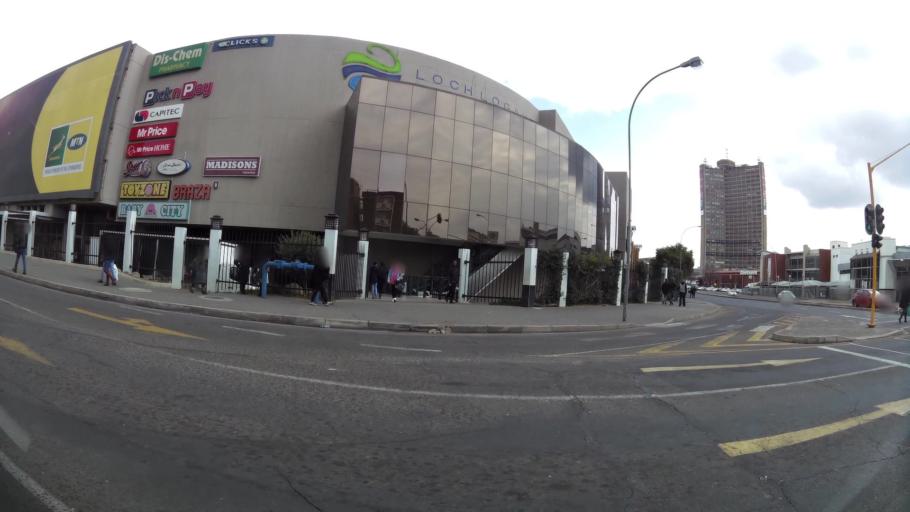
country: ZA
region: Orange Free State
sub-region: Mangaung Metropolitan Municipality
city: Bloemfontein
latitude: -29.1141
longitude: 26.2119
